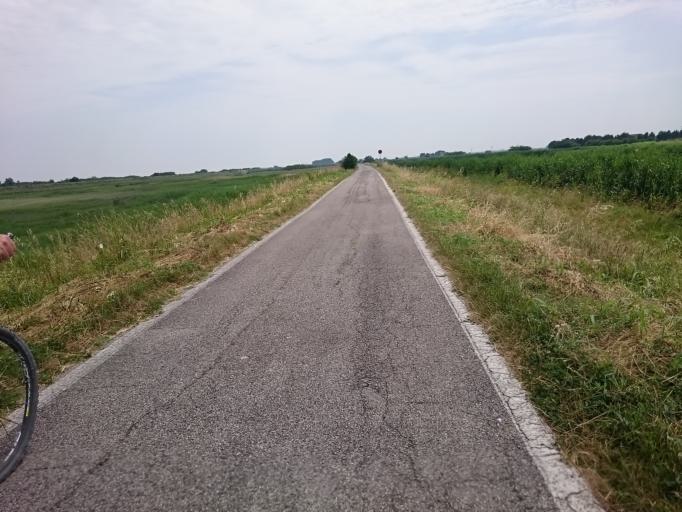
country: IT
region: Veneto
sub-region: Provincia di Venezia
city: Valli
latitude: 45.1900
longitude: 12.2162
